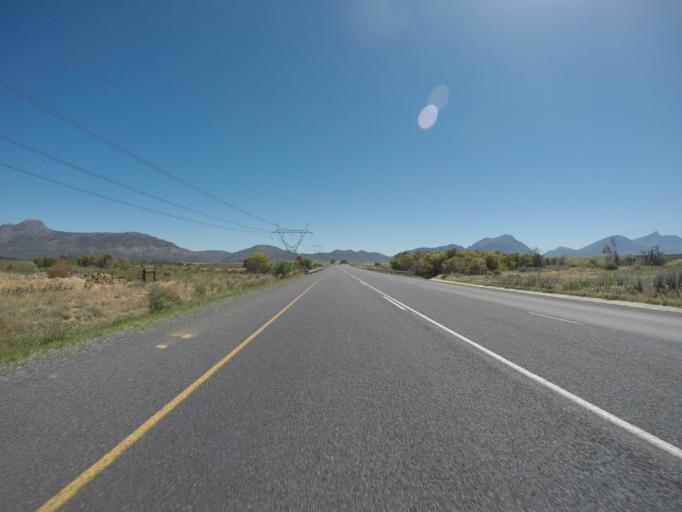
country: ZA
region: Western Cape
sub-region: Cape Winelands District Municipality
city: Ceres
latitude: -33.3245
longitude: 19.1480
